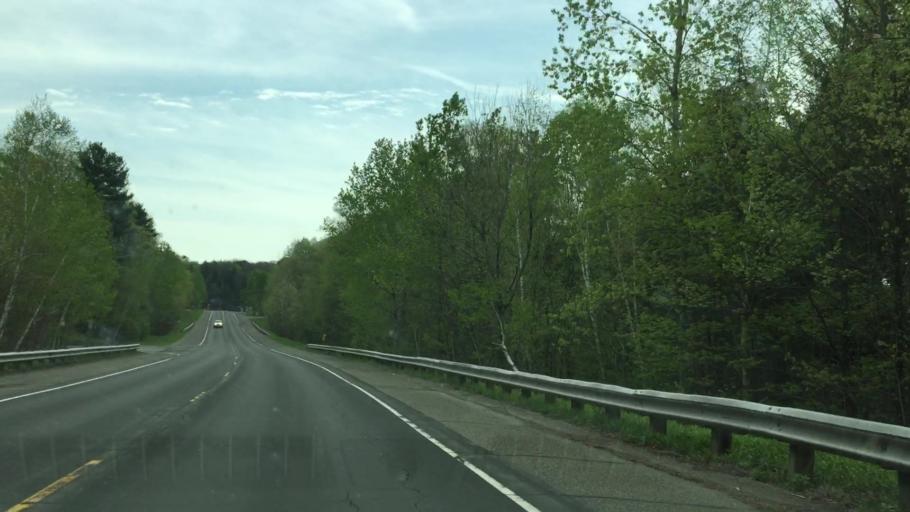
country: US
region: Massachusetts
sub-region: Berkshire County
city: Pittsfield
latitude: 42.4125
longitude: -73.2703
